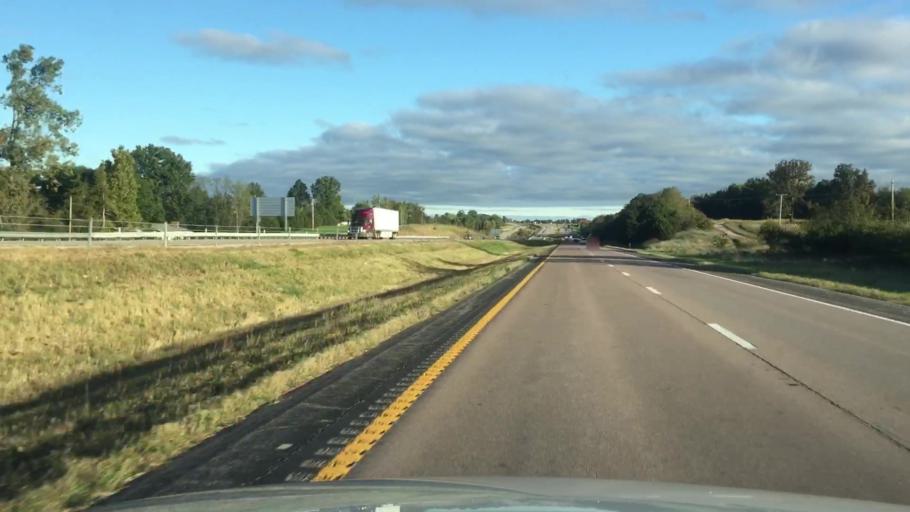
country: US
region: Missouri
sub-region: Boone County
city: Ashland
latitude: 38.8469
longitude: -92.2491
